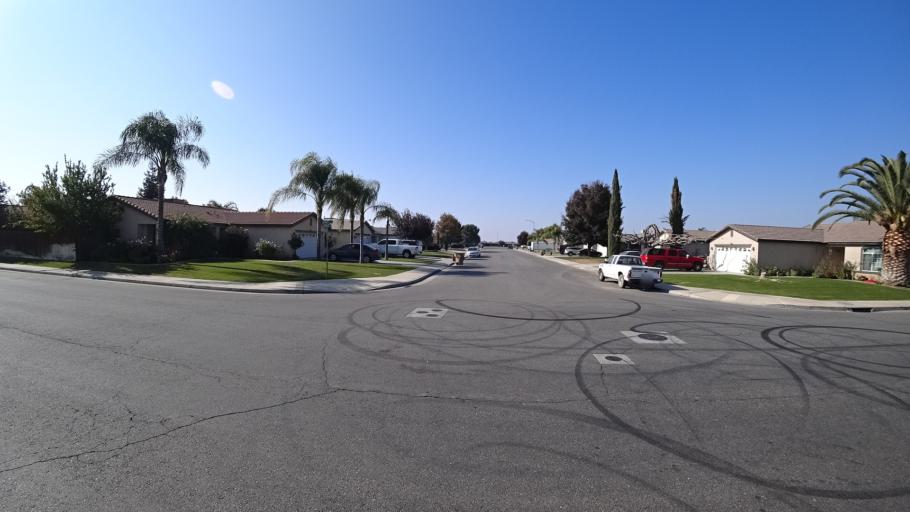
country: US
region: California
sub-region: Kern County
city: Greenfield
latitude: 35.2800
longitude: -119.0173
